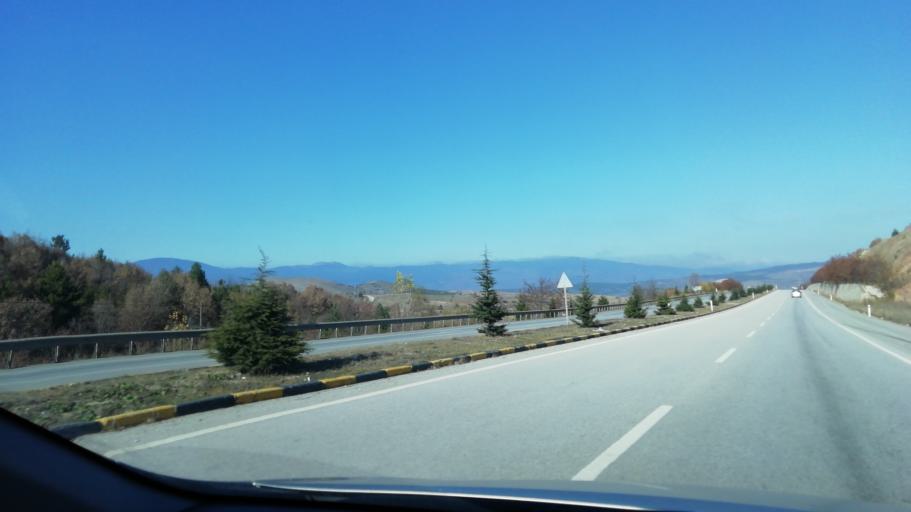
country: TR
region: Karabuk
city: Gozyeri
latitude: 40.8951
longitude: 32.5798
